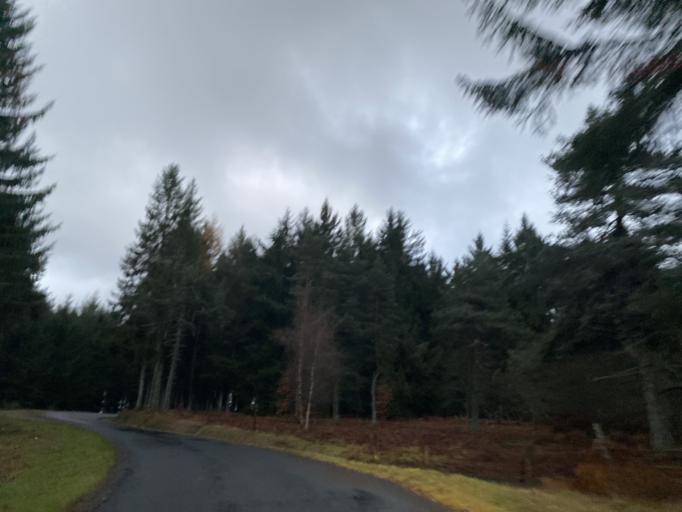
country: FR
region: Auvergne
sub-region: Departement du Puy-de-Dome
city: Cunlhat
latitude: 45.5545
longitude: 3.5723
